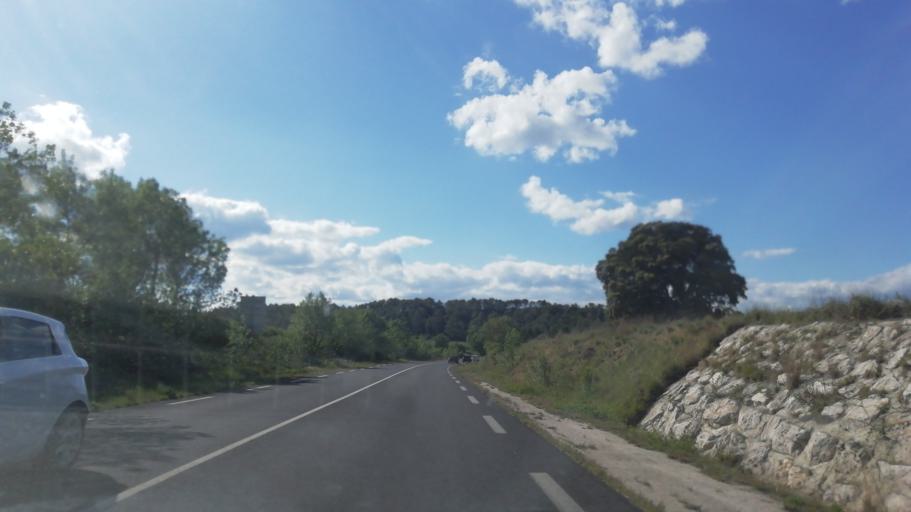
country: FR
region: Languedoc-Roussillon
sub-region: Departement de l'Herault
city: Saint-Clement-de-Riviere
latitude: 43.7000
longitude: 3.8233
